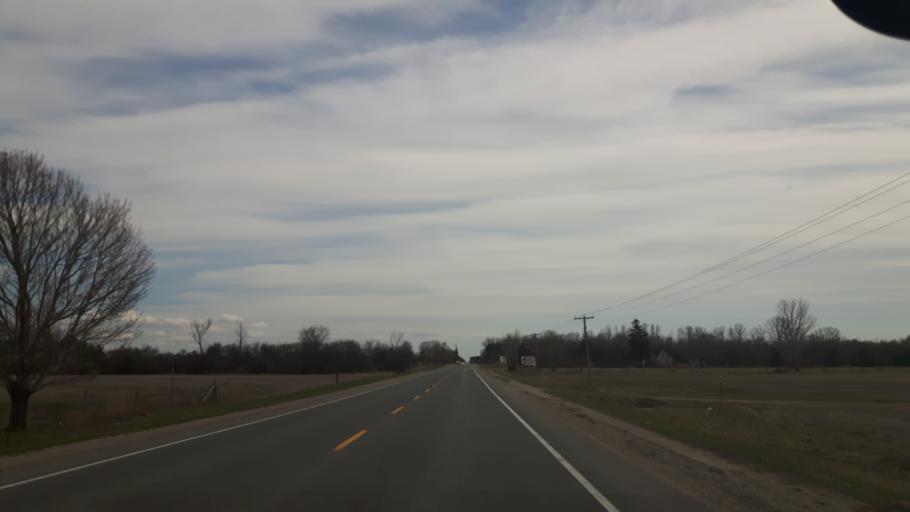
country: CA
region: Ontario
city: Goderich
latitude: 43.7063
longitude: -81.7057
